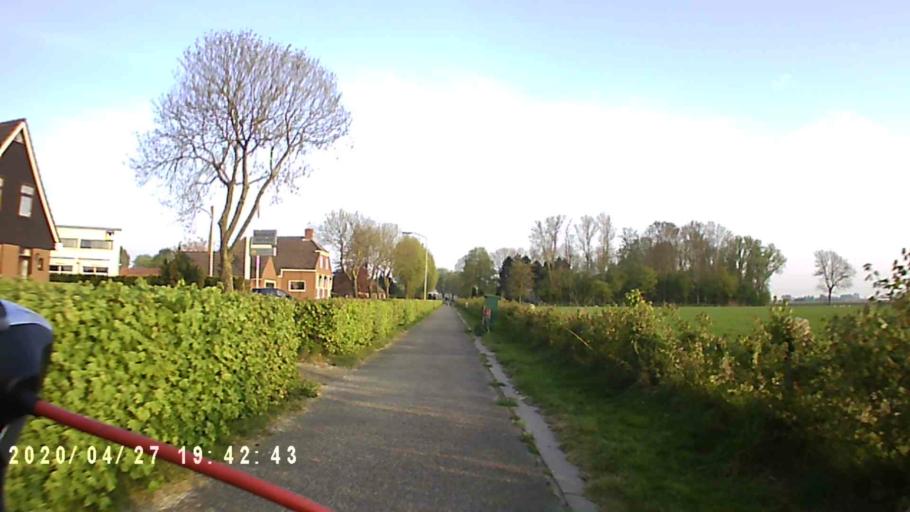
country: NL
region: Groningen
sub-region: Gemeente Winsum
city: Winsum
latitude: 53.3579
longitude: 6.4641
